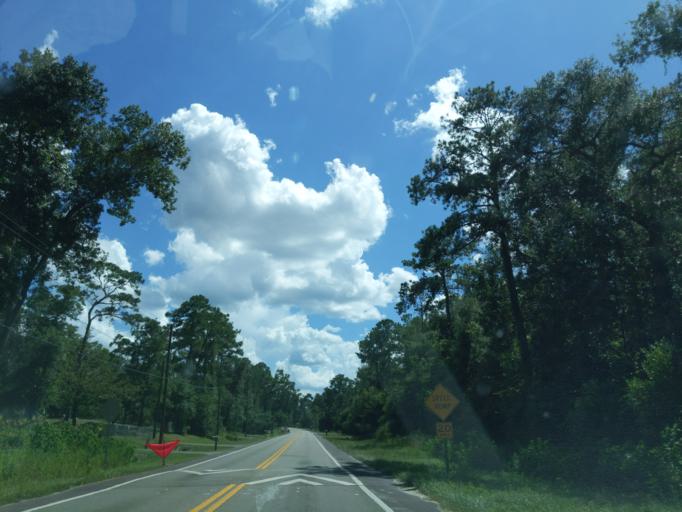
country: US
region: Florida
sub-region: Leon County
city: Tallahassee
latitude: 30.4111
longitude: -84.3286
